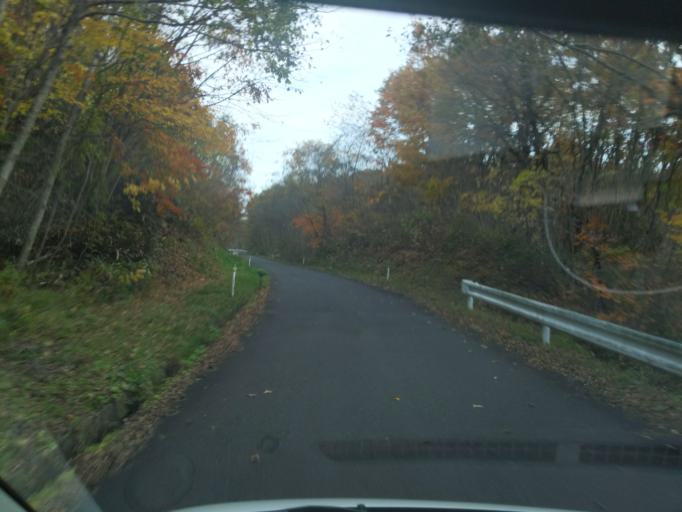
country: JP
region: Iwate
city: Ichinoseki
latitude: 38.9945
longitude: 141.0055
